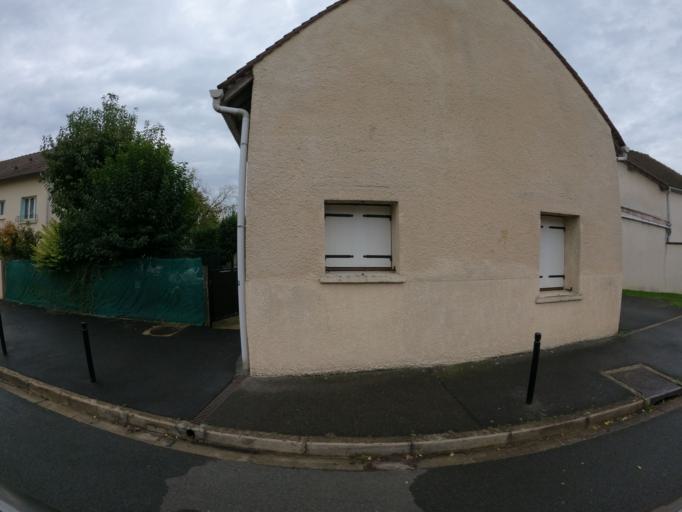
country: FR
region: Ile-de-France
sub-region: Departement de Seine-et-Marne
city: Serris
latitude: 48.8424
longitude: 2.7881
